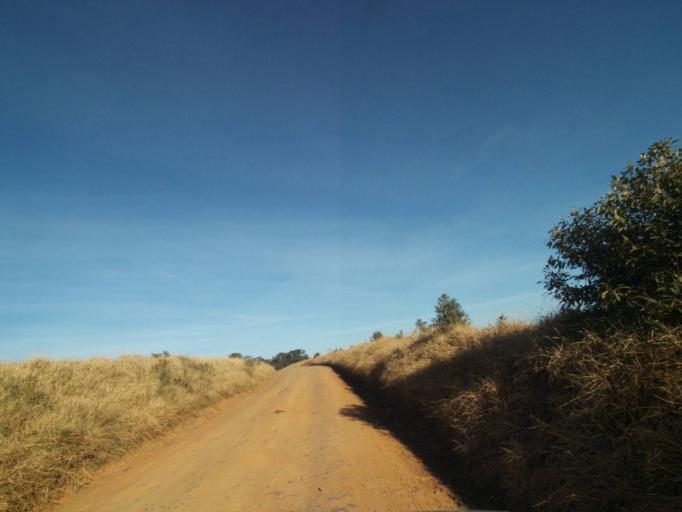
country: BR
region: Parana
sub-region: Telemaco Borba
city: Telemaco Borba
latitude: -24.5309
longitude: -50.6317
